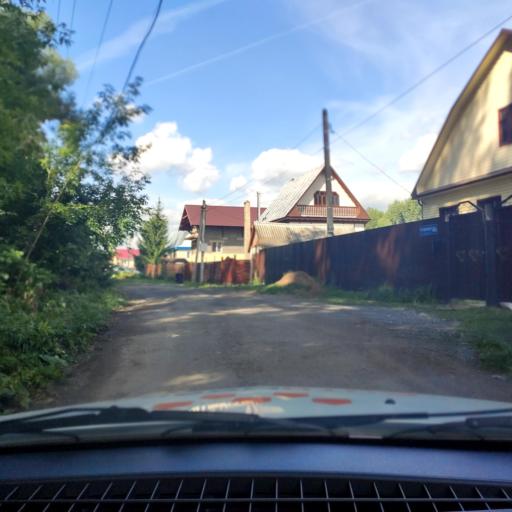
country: RU
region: Bashkortostan
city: Ufa
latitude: 54.7100
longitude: 55.9373
